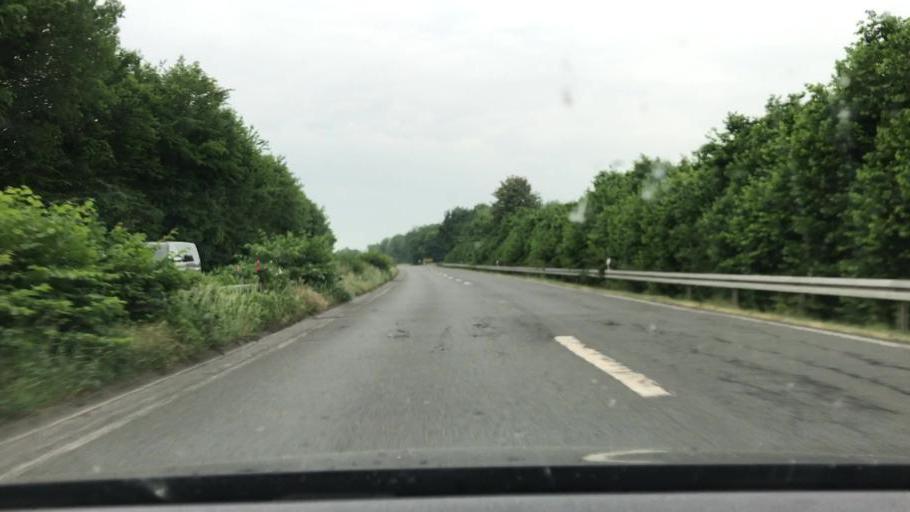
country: DE
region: North Rhine-Westphalia
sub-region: Regierungsbezirk Munster
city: Recklinghausen
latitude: 51.6340
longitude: 7.1969
